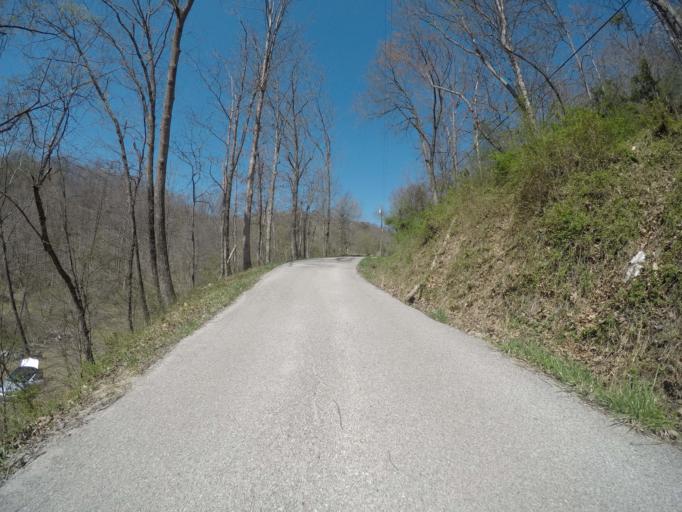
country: US
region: West Virginia
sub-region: Kanawha County
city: Charleston
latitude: 38.4079
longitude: -81.5892
